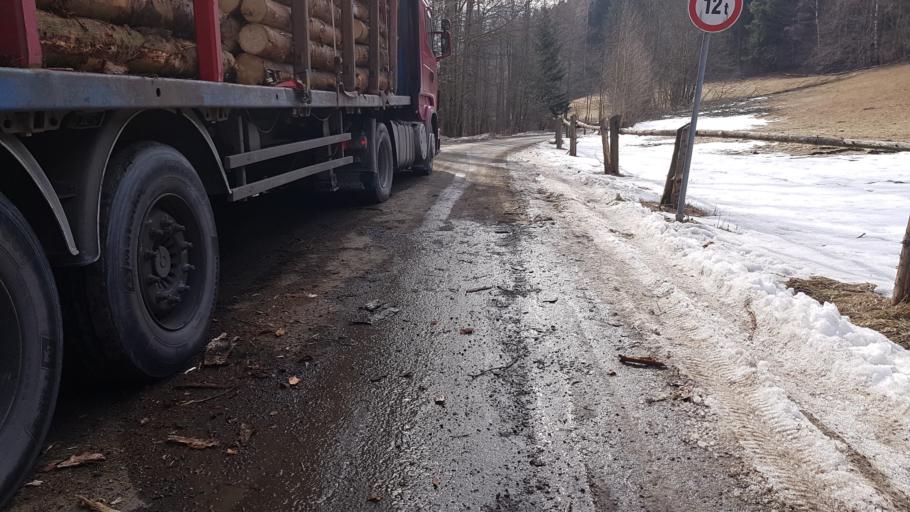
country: CZ
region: Olomoucky
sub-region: Okres Jesenik
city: Jesenik
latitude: 50.2273
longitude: 17.2297
